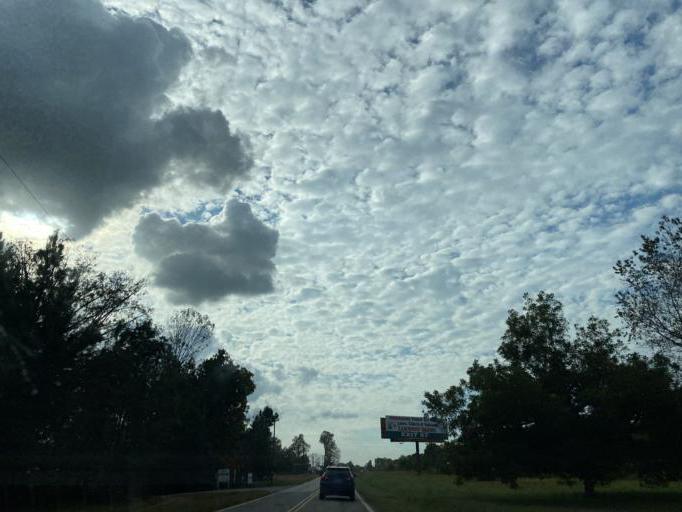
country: US
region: South Carolina
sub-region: Cherokee County
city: Gaffney
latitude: 35.0755
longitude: -81.7329
